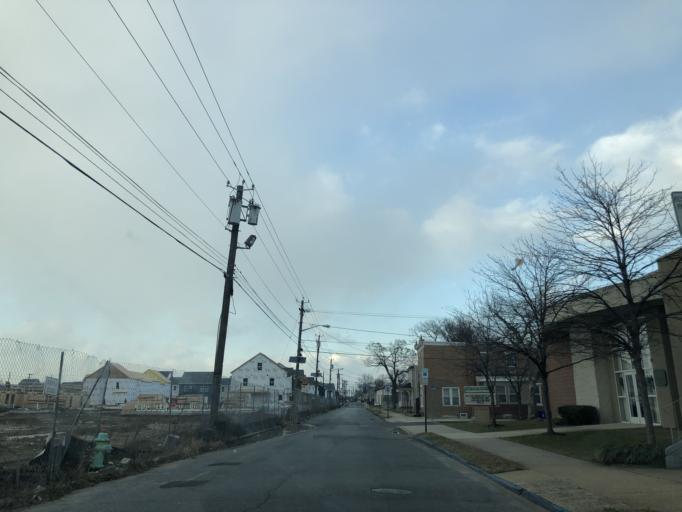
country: US
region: New Jersey
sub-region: Camden County
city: Camden
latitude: 39.9203
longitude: -75.1086
